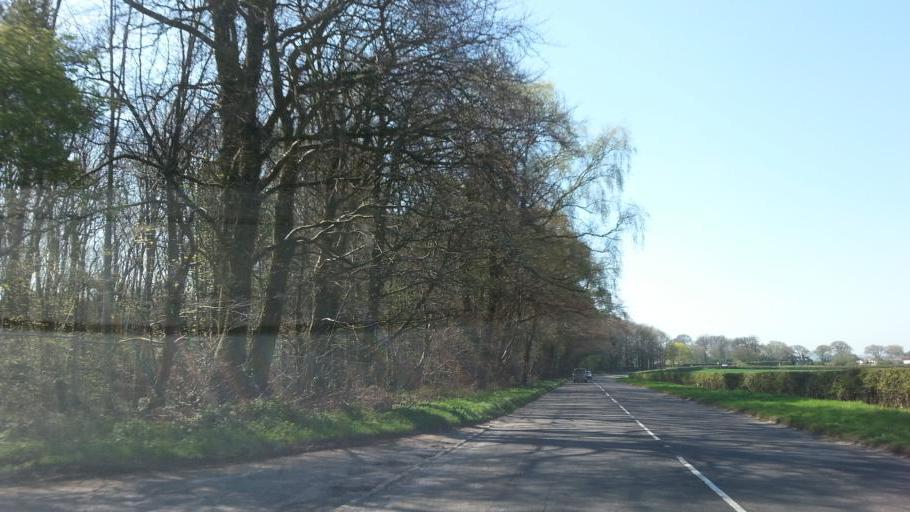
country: GB
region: England
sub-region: Staffordshire
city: Stafford
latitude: 52.8322
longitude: -2.0607
